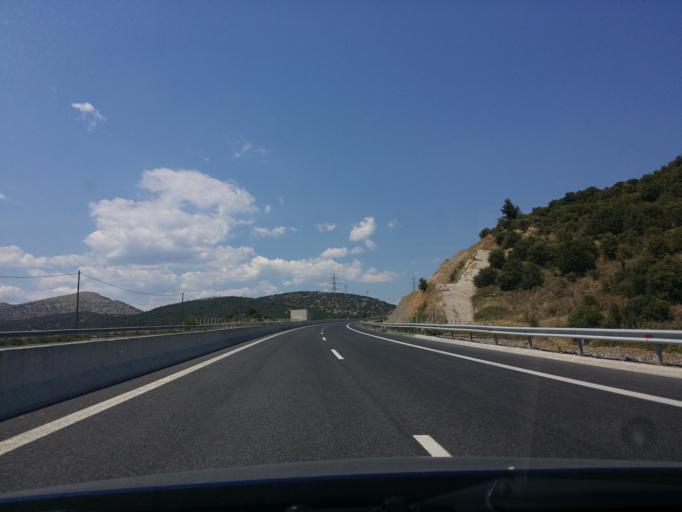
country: GR
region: Peloponnese
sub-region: Nomos Arkadias
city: Tripoli
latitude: 37.4275
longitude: 22.3106
